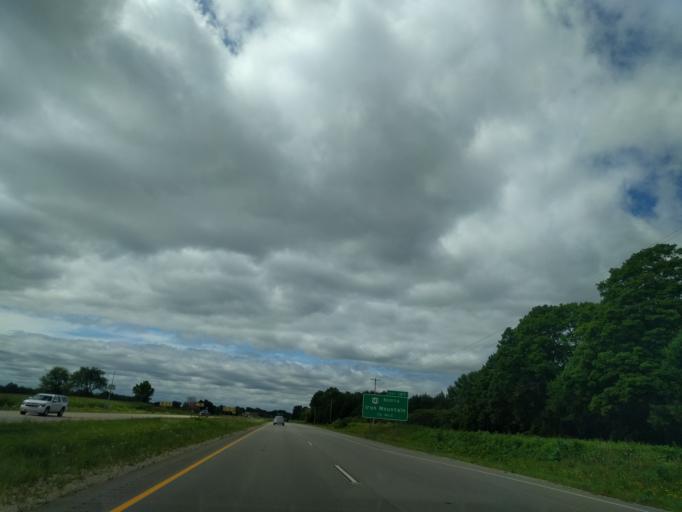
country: US
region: Wisconsin
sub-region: Oconto County
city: Oconto Falls
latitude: 44.7951
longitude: -88.0321
